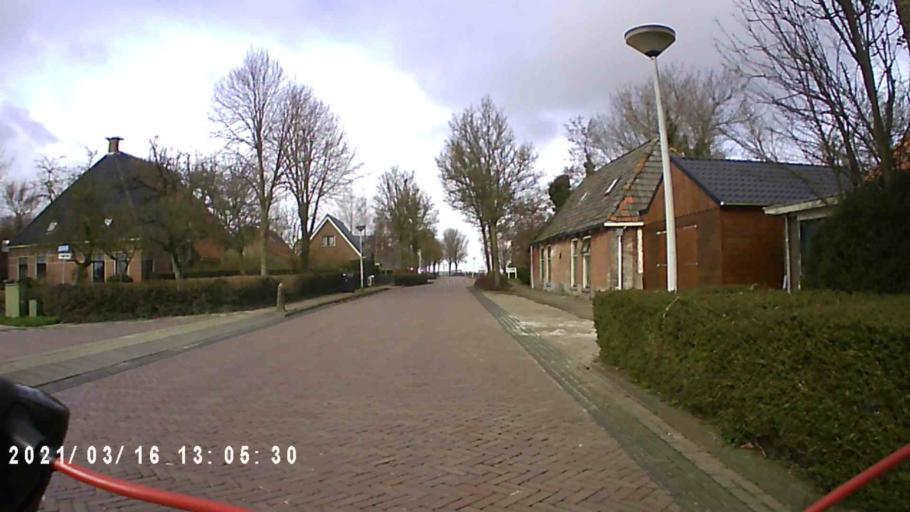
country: NL
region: Friesland
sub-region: Menameradiel
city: Berltsum
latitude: 53.2522
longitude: 5.6270
